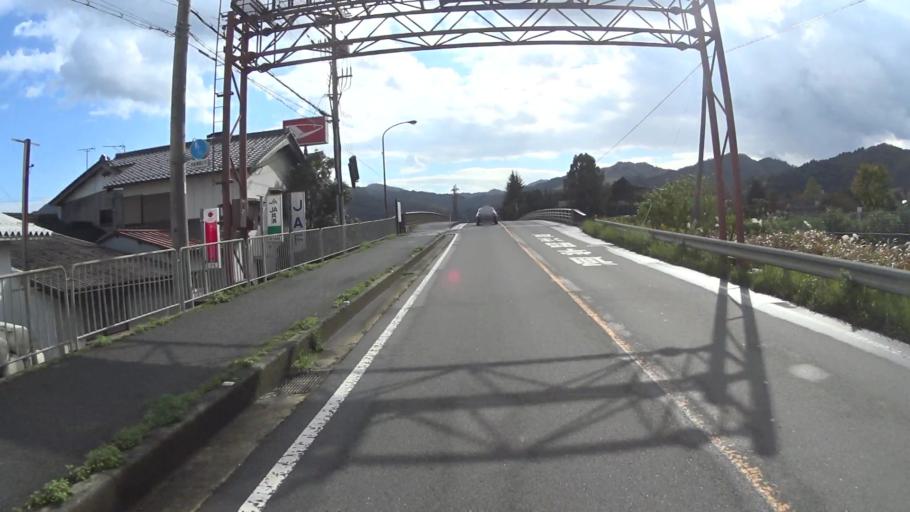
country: JP
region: Kyoto
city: Miyazu
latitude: 35.5606
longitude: 135.1535
